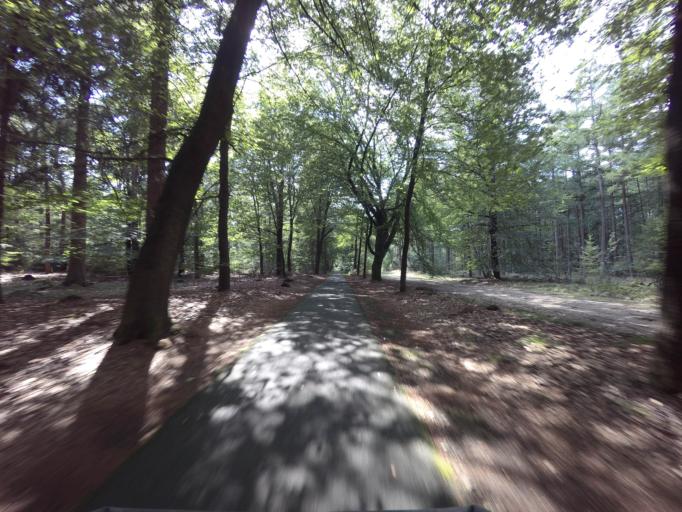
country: NL
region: Drenthe
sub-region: Gemeente Westerveld
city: Dwingeloo
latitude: 52.8248
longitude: 6.4650
